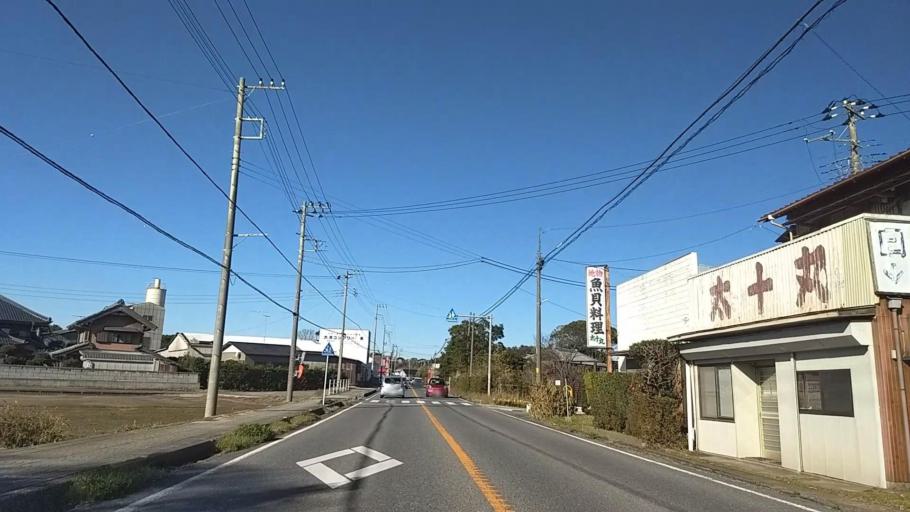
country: JP
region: Chiba
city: Ohara
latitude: 35.3199
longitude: 140.4031
